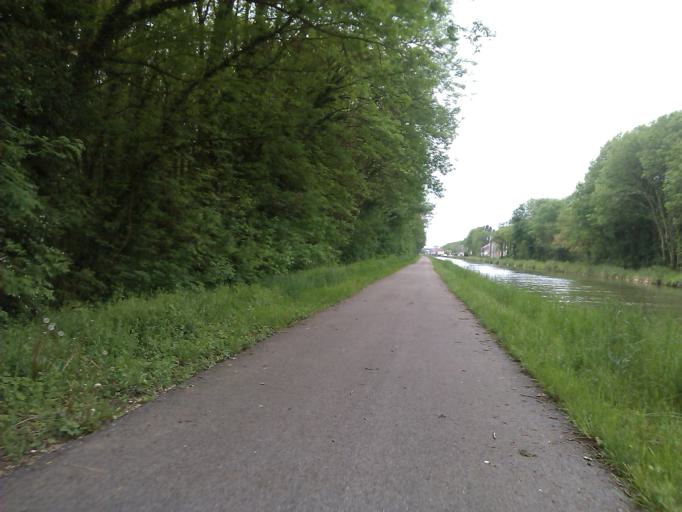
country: FR
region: Franche-Comte
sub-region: Departement du Jura
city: Damparis
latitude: 47.0595
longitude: 5.4239
